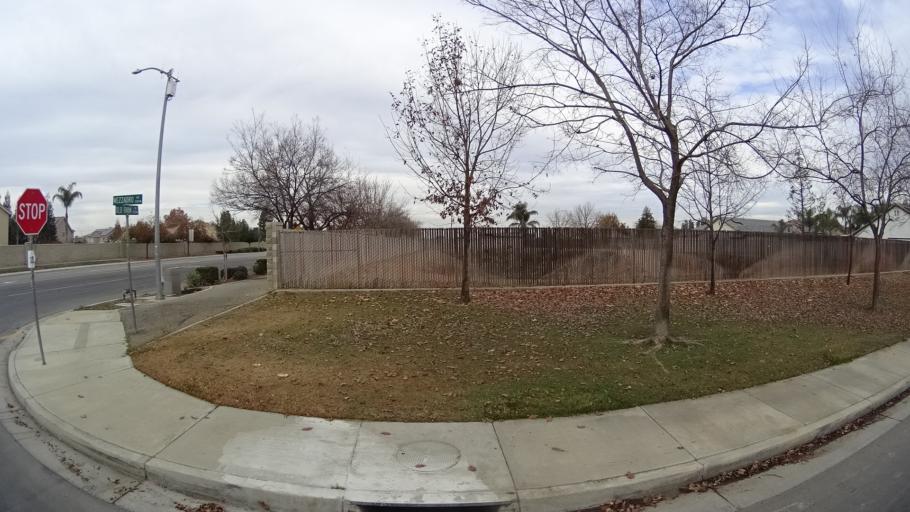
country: US
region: California
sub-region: Kern County
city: Rosedale
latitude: 35.4253
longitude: -119.1363
